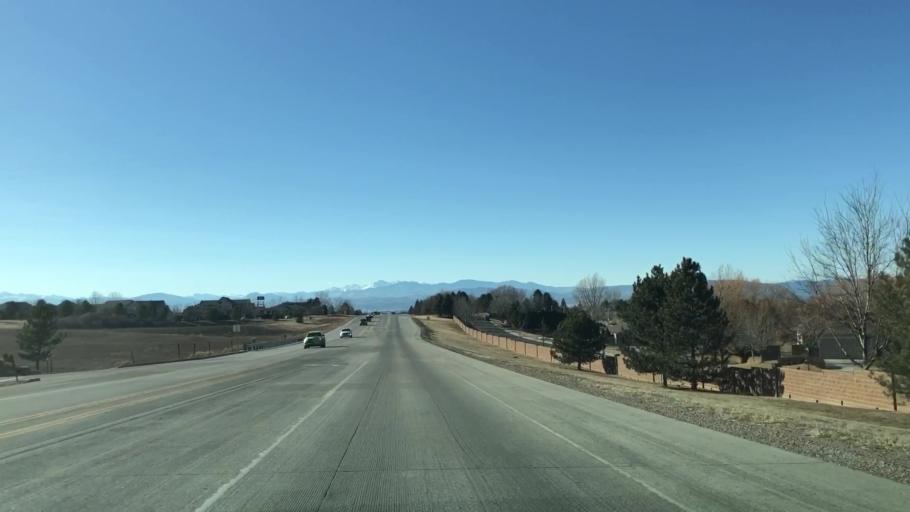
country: US
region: Colorado
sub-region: Weld County
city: Windsor
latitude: 40.4794
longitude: -104.9697
